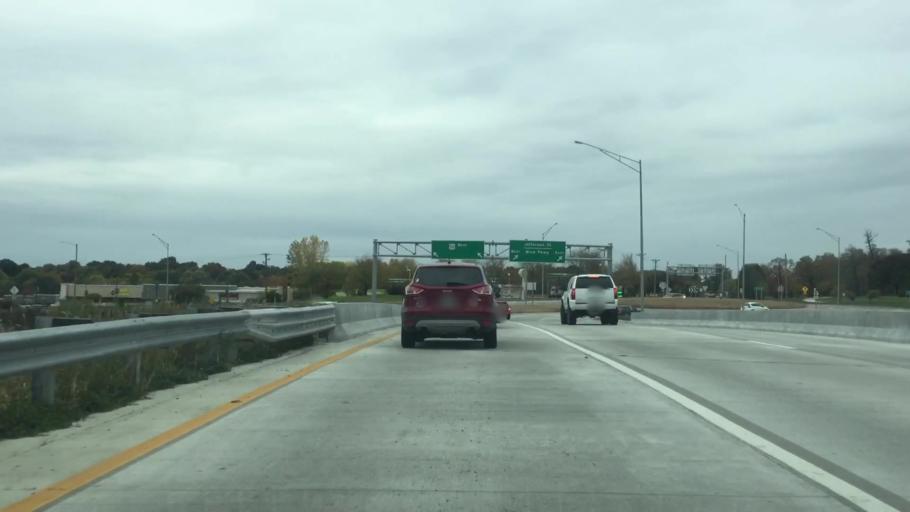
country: US
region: Missouri
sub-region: Jackson County
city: Lees Summit
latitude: 38.9029
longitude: -94.3776
